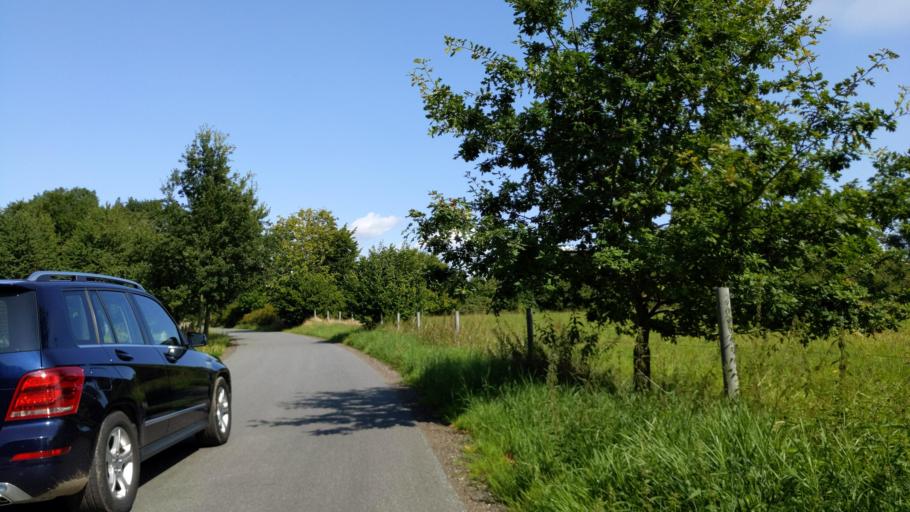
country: DE
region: Schleswig-Holstein
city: Bosdorf
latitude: 54.1632
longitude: 10.4908
